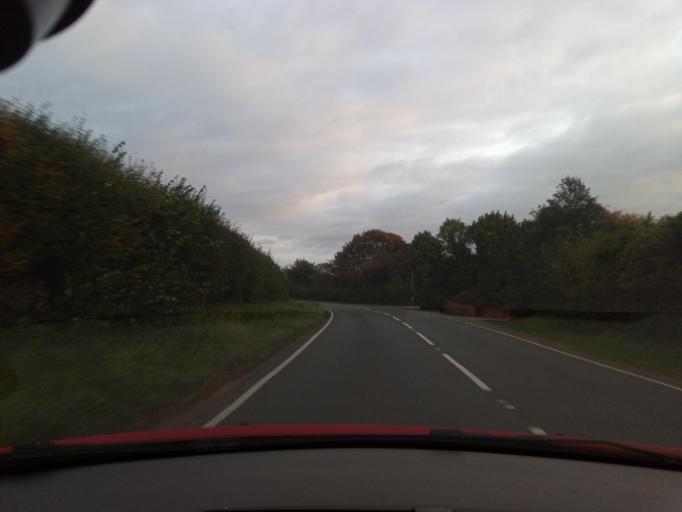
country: GB
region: England
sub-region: Essex
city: West Mersea
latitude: 51.7873
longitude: 0.9206
